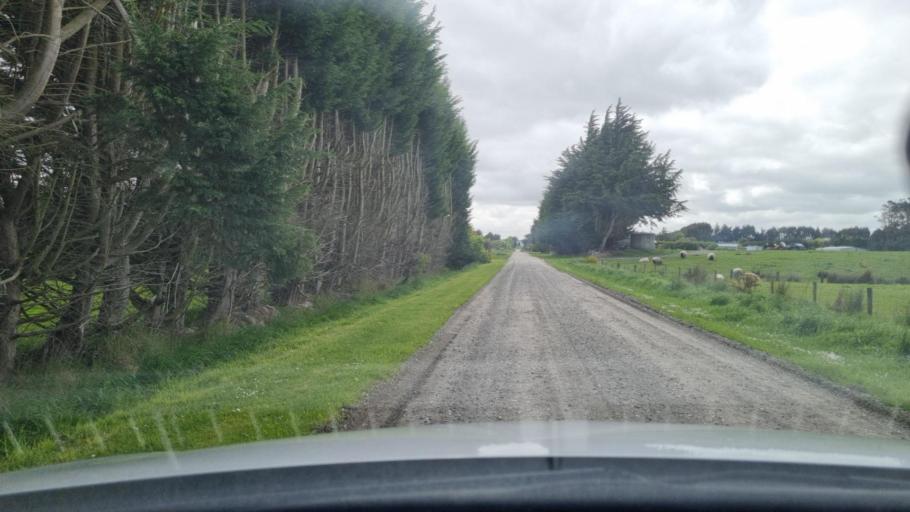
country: NZ
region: Southland
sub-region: Invercargill City
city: Invercargill
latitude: -46.4383
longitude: 168.3897
